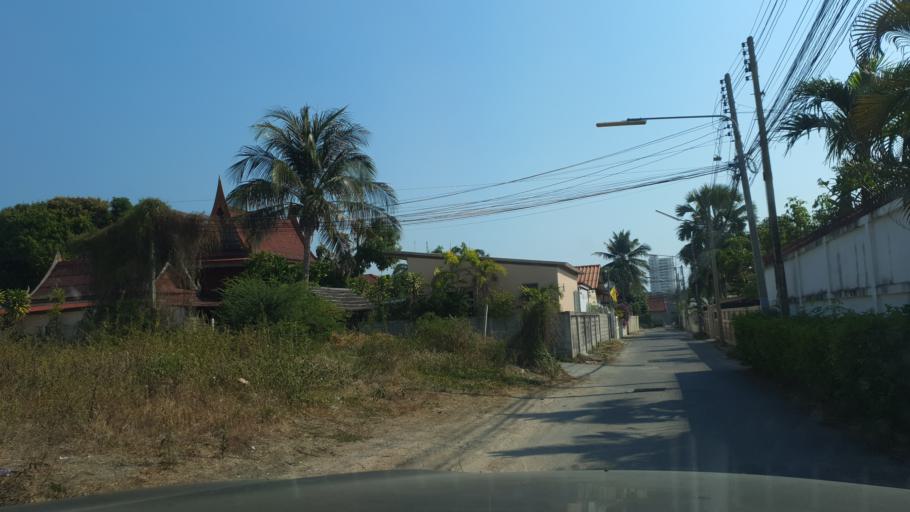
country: TH
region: Prachuap Khiri Khan
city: Hua Hin
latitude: 12.5521
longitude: 99.9550
